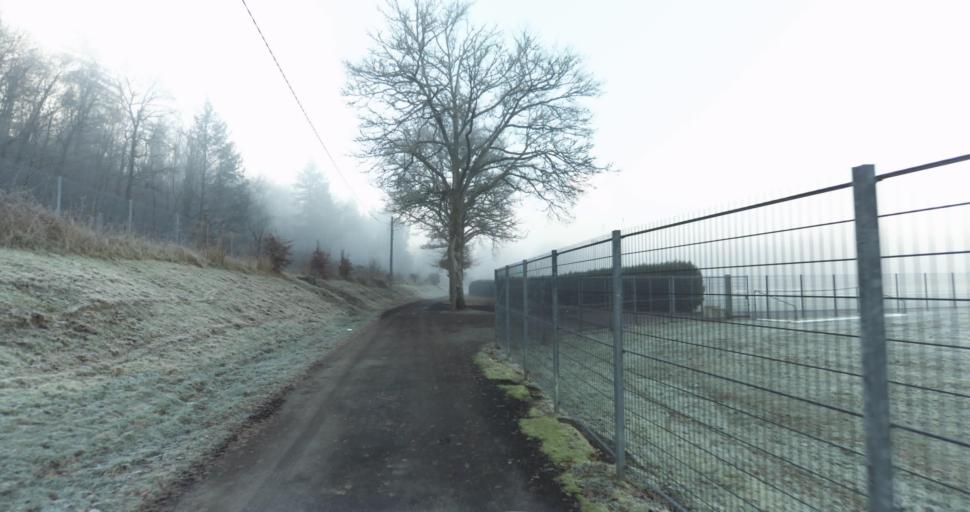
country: FR
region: Limousin
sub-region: Departement de la Haute-Vienne
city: Aixe-sur-Vienne
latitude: 45.7972
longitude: 1.1539
